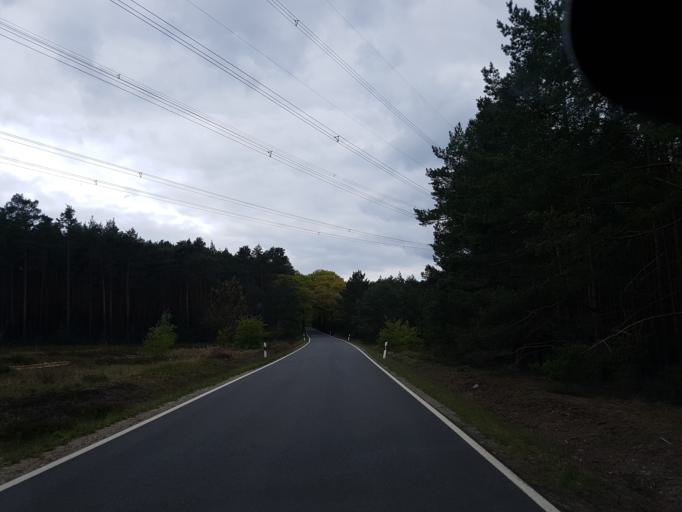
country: DE
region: Brandenburg
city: Bronkow
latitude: 51.6386
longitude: 13.9552
